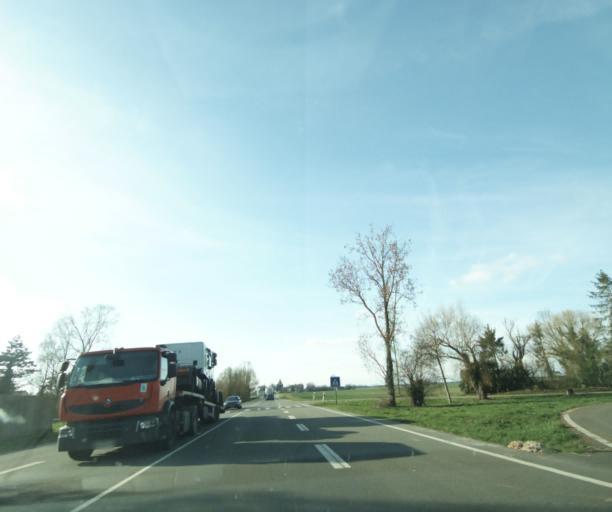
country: FR
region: Ile-de-France
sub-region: Departement des Yvelines
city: Ablis
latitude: 48.4650
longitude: 1.8779
